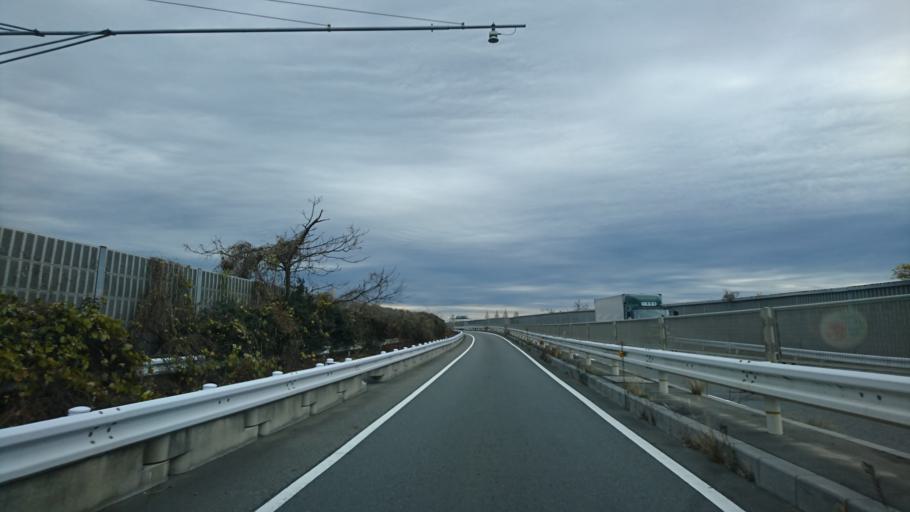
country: JP
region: Shizuoka
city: Kanaya
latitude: 34.8374
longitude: 138.1258
